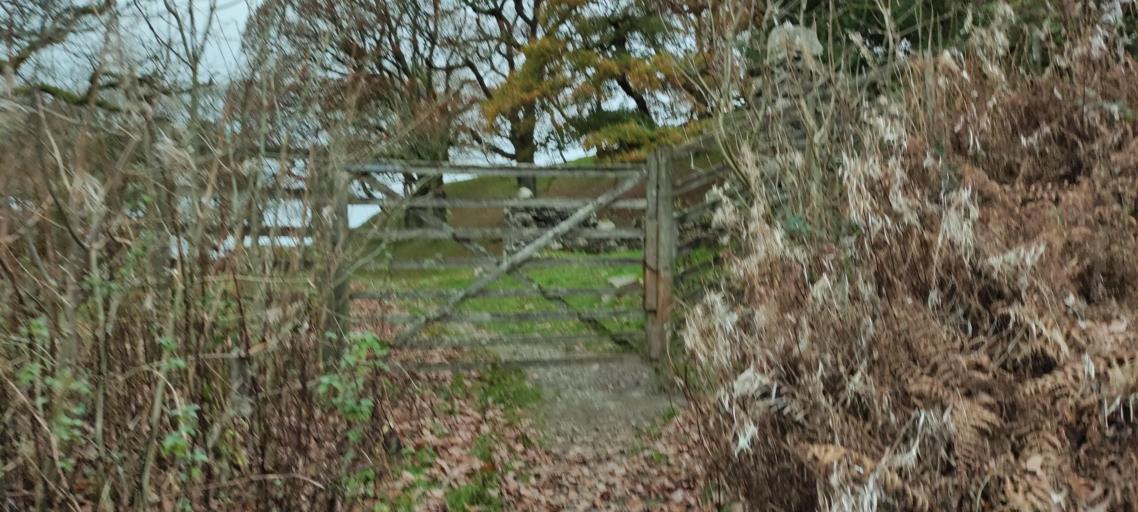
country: GB
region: England
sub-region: Cumbria
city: Cockermouth
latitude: 54.6501
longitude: -3.2501
